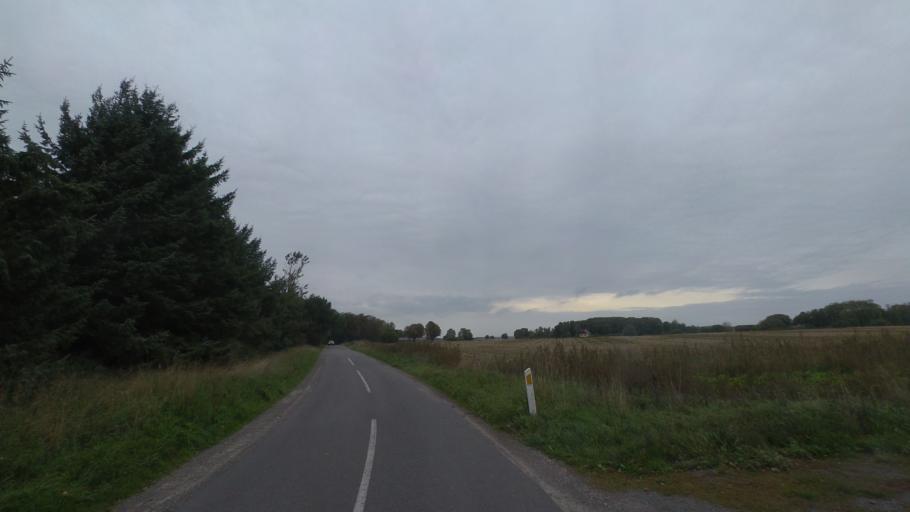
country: DK
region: Capital Region
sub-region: Bornholm Kommune
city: Akirkeby
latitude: 55.0055
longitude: 14.9927
